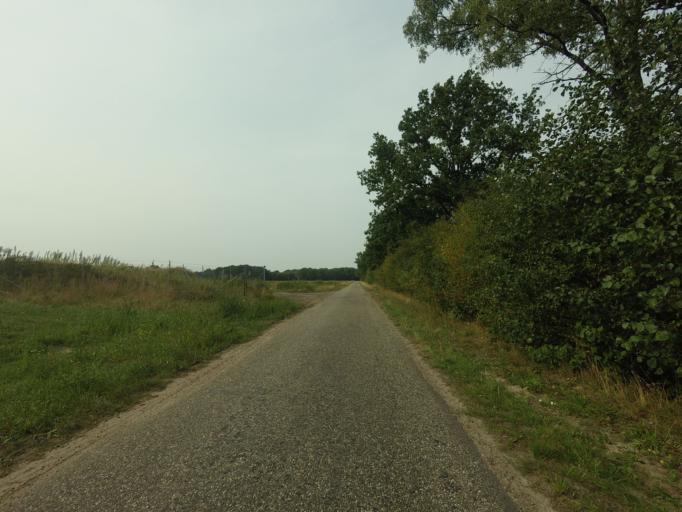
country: NL
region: Drenthe
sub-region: Gemeente Tynaarlo
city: Vries
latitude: 53.1082
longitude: 6.5456
